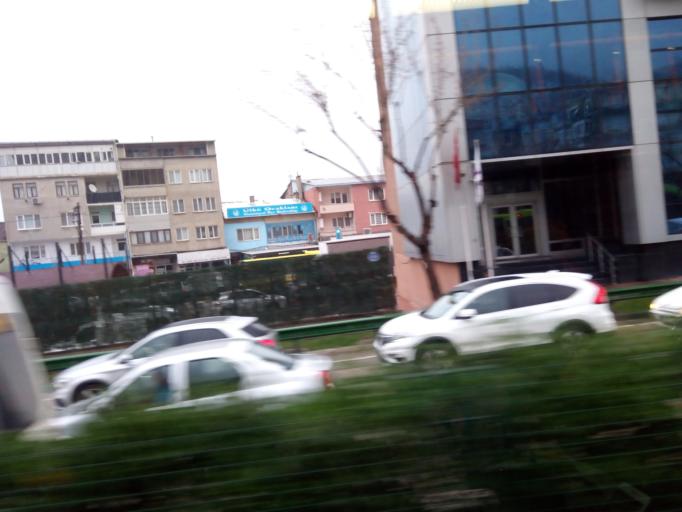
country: TR
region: Bursa
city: Yildirim
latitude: 40.2028
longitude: 29.0343
